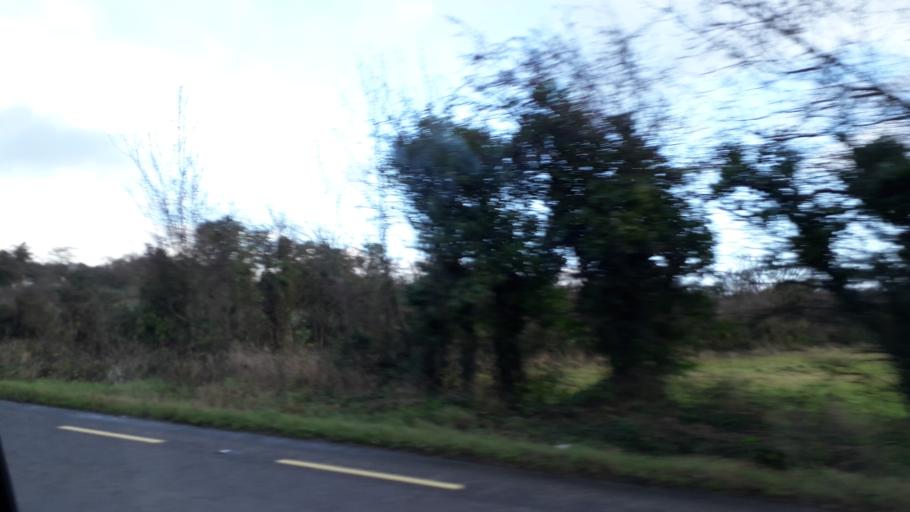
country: IE
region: Leinster
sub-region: An Mhi
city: Slane
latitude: 53.7498
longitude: -6.5039
